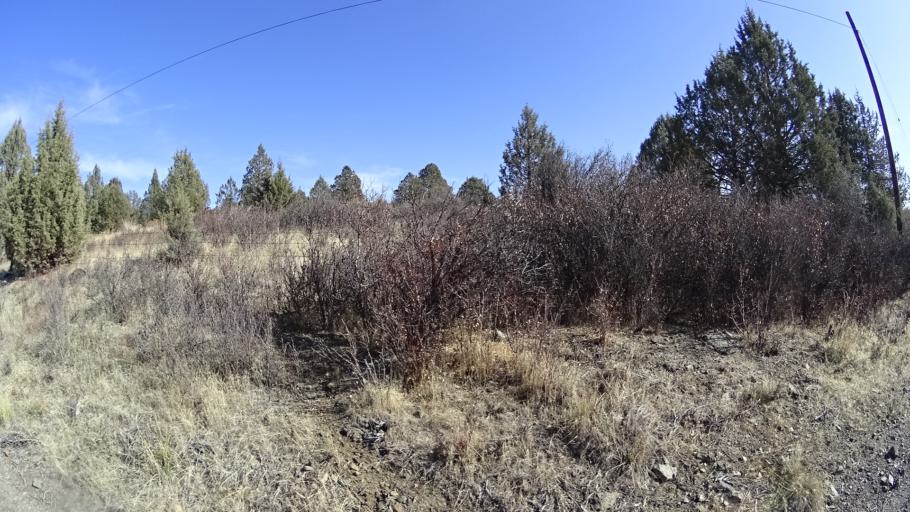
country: US
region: California
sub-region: Siskiyou County
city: Yreka
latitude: 41.7741
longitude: -122.5931
